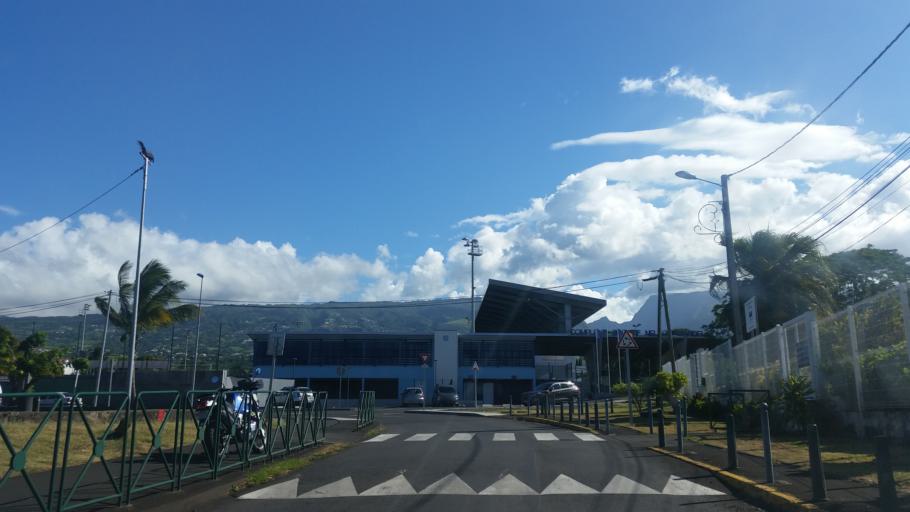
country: RE
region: Reunion
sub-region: Reunion
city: Sainte-Marie
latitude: -20.9015
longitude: 55.5210
